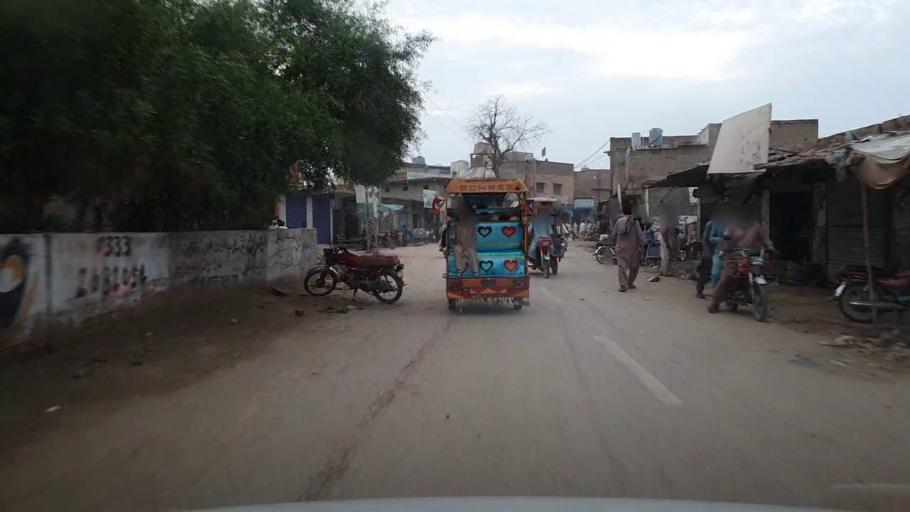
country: PK
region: Sindh
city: Naushahro Firoz
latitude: 26.8397
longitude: 68.1201
